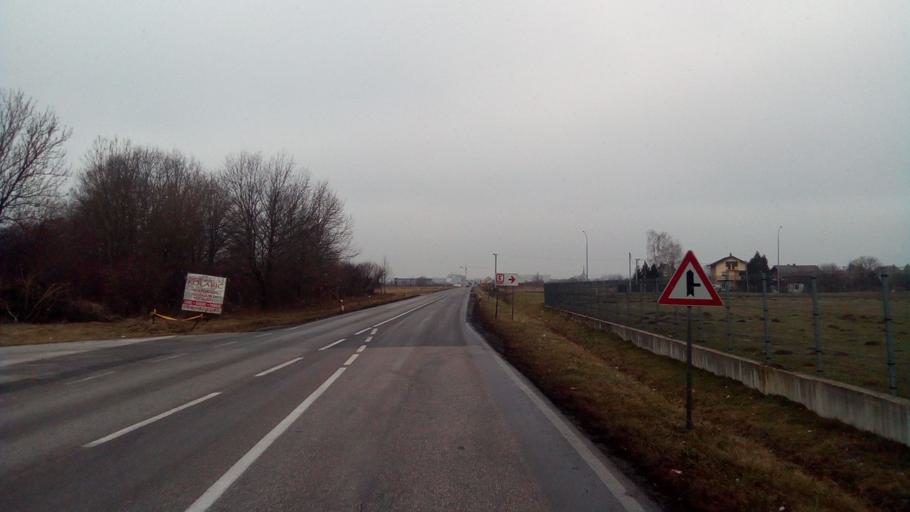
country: HR
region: Zagrebacka
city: Jastrebarsko
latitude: 45.6462
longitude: 15.6731
